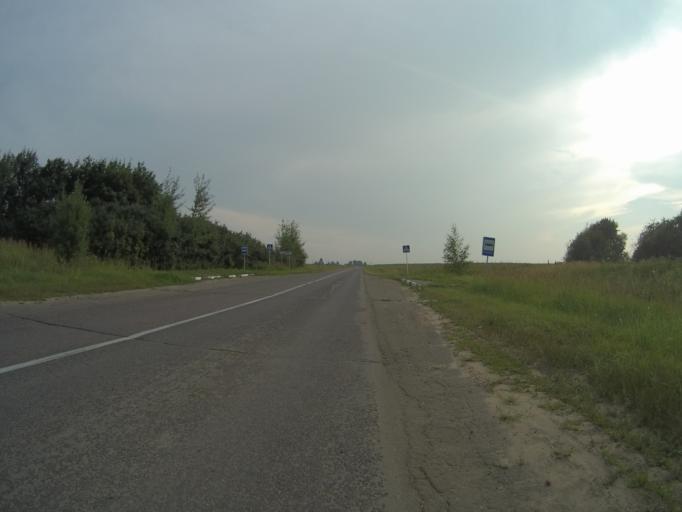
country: RU
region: Ivanovo
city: Gavrilov Posad
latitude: 56.3522
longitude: 40.2162
